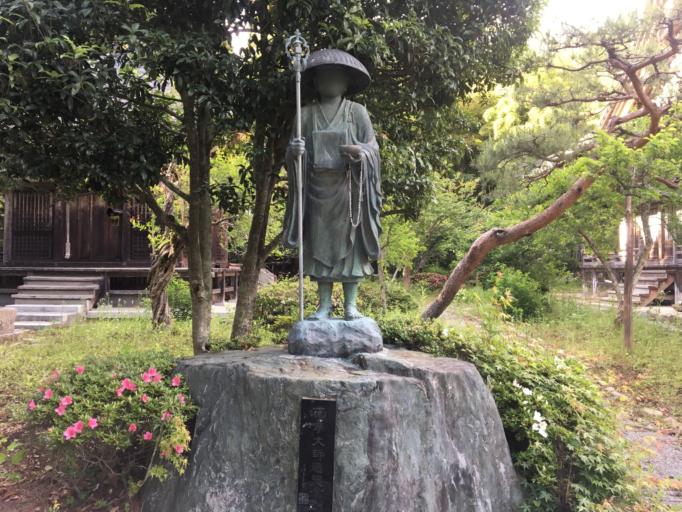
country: JP
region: Fukushima
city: Namie
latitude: 37.4975
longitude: 141.0142
